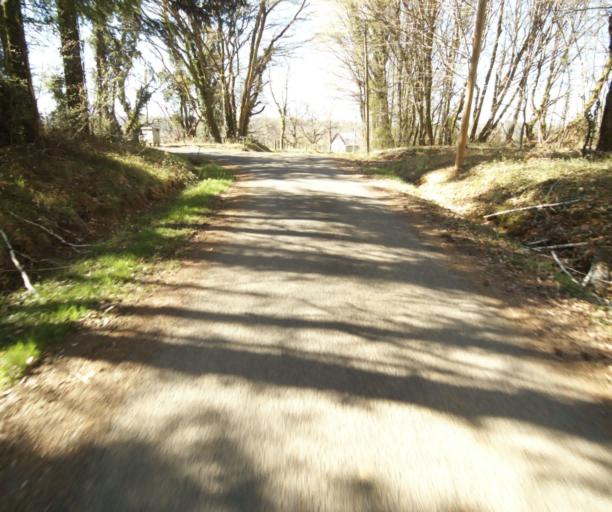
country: FR
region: Limousin
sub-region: Departement de la Correze
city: Chamboulive
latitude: 45.4109
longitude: 1.6864
